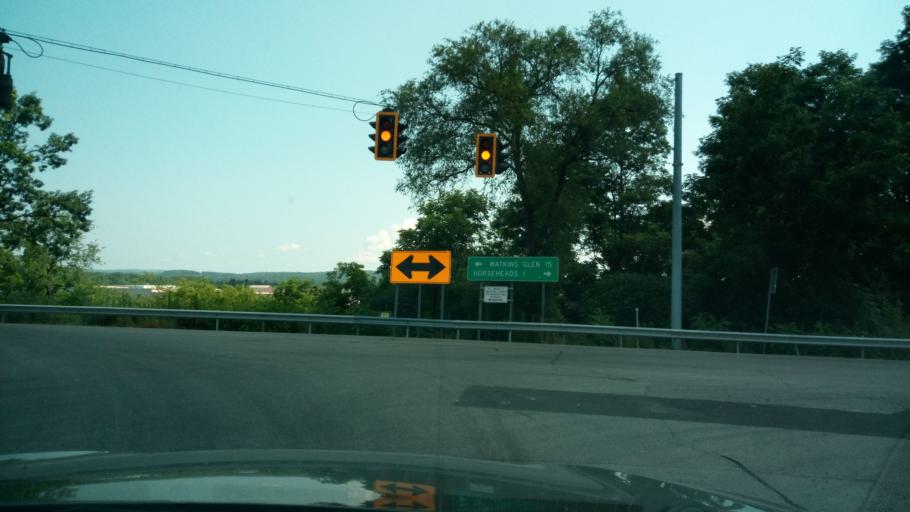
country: US
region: New York
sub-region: Chemung County
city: Horseheads
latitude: 42.1814
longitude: -76.8318
